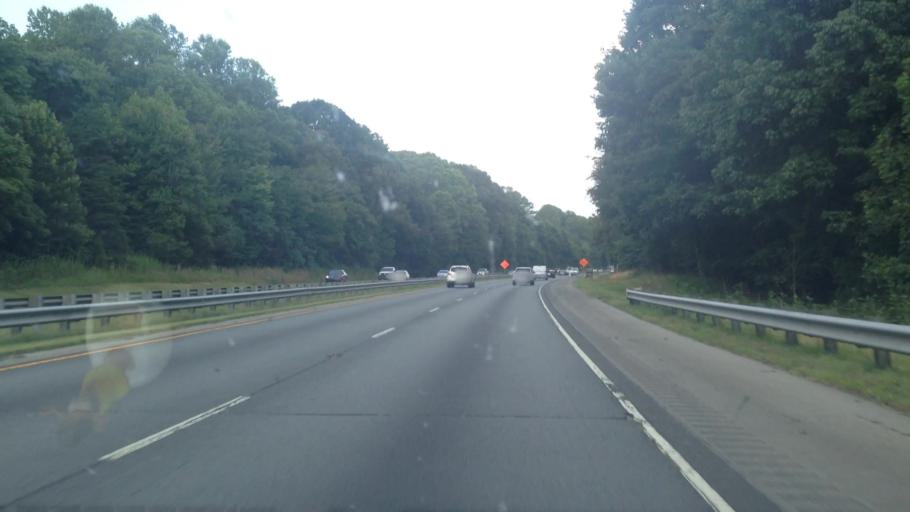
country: US
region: North Carolina
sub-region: Forsyth County
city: Walkertown
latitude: 36.1138
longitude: -80.1570
